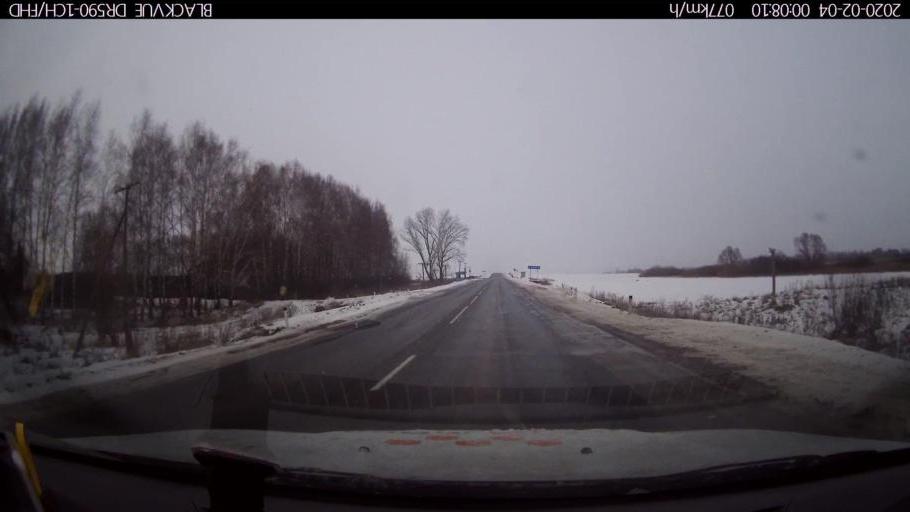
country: RU
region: Nizjnij Novgorod
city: Dal'neye Konstantinovo
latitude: 55.8679
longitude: 44.1334
